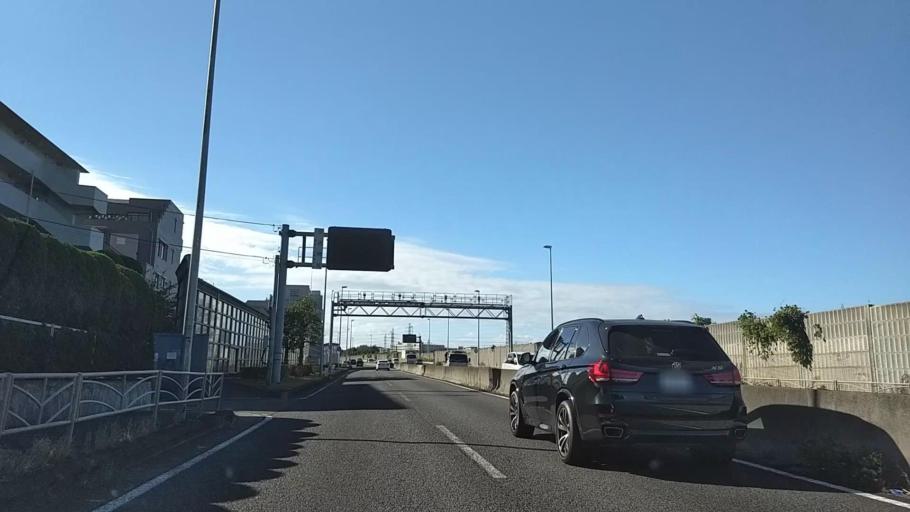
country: JP
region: Kanagawa
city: Fujisawa
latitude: 35.4080
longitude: 139.5297
